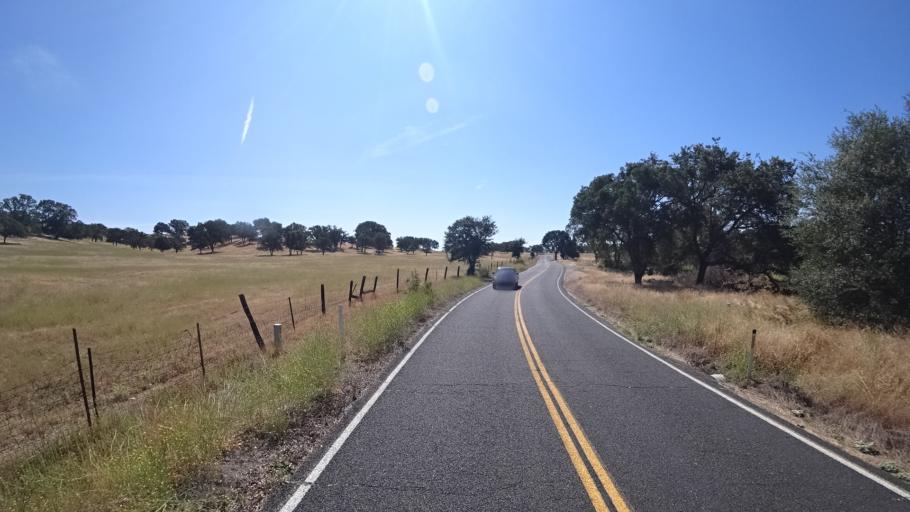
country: US
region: California
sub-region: Calaveras County
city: Rancho Calaveras
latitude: 38.1079
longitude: -120.9248
